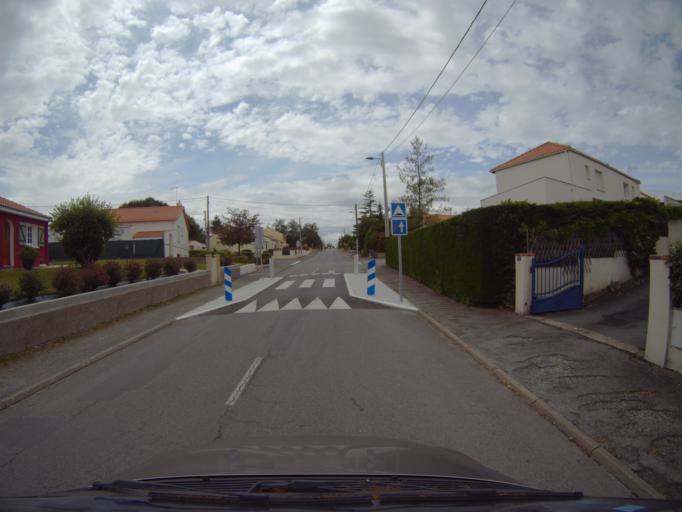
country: FR
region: Pays de la Loire
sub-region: Departement de la Loire-Atlantique
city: Montbert
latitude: 47.0583
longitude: -1.4911
